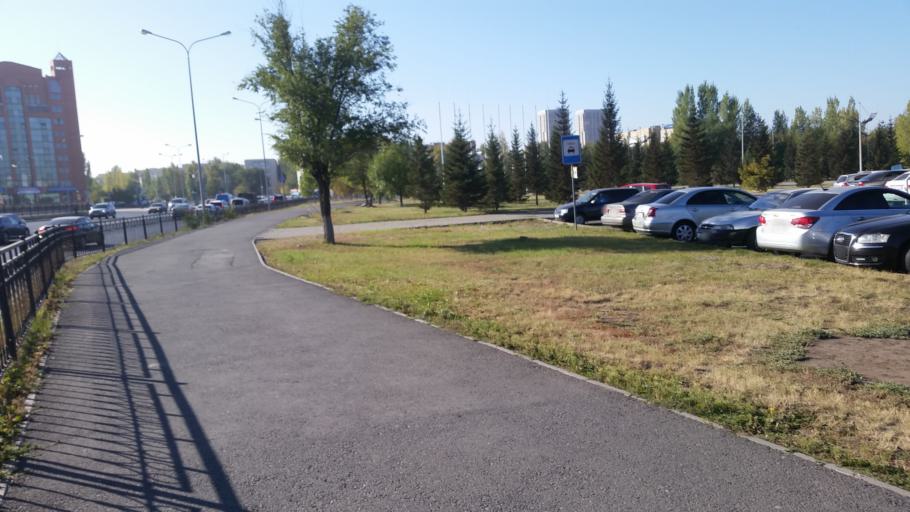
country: KZ
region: Astana Qalasy
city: Astana
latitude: 51.1559
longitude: 71.4667
